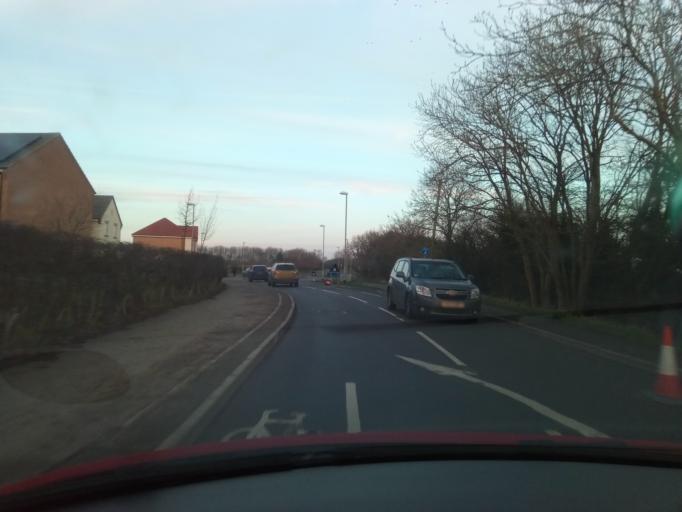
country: GB
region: England
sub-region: Leicestershire
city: Sileby
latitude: 52.7423
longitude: -1.0999
